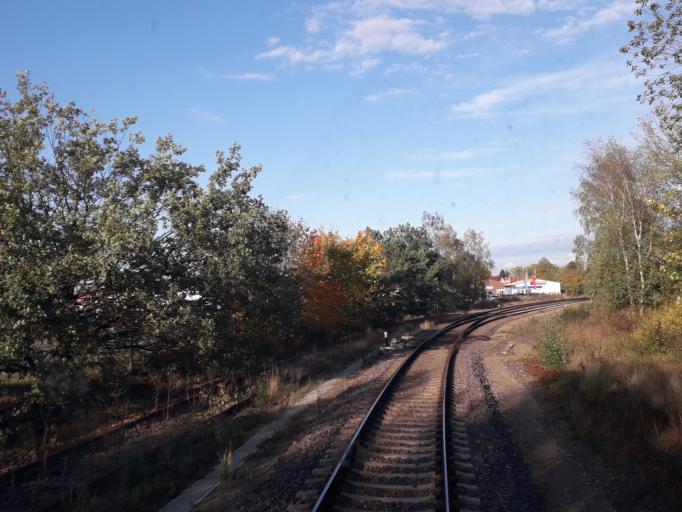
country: DE
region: Brandenburg
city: Perleberg
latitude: 53.0673
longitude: 11.8432
